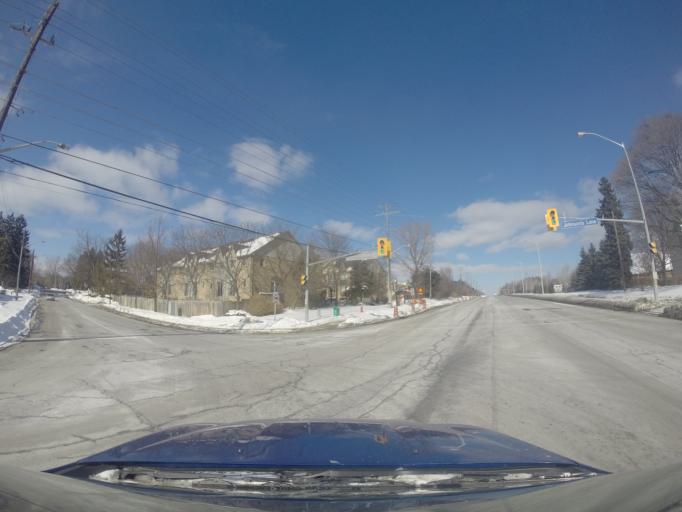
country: CA
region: Ontario
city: Mississauga
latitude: 43.5220
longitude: -79.6179
